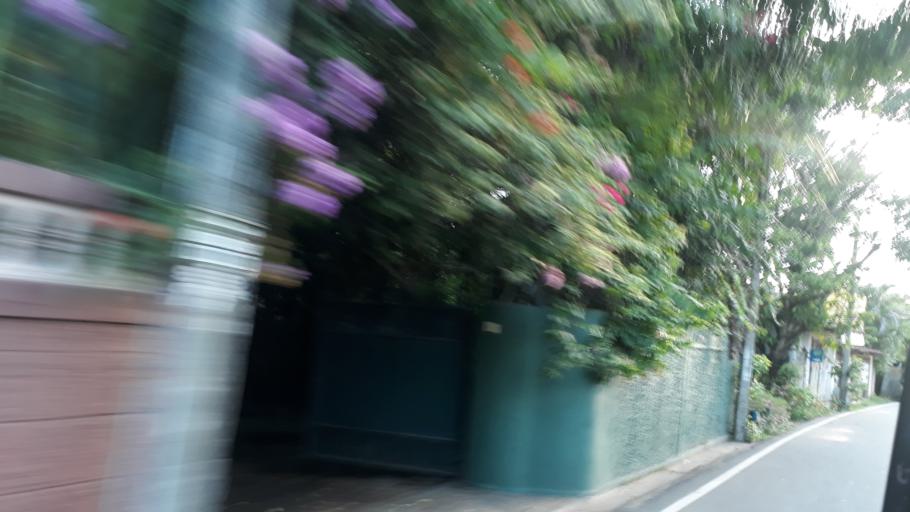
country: LK
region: Western
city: Gampaha
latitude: 7.1021
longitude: 79.9890
